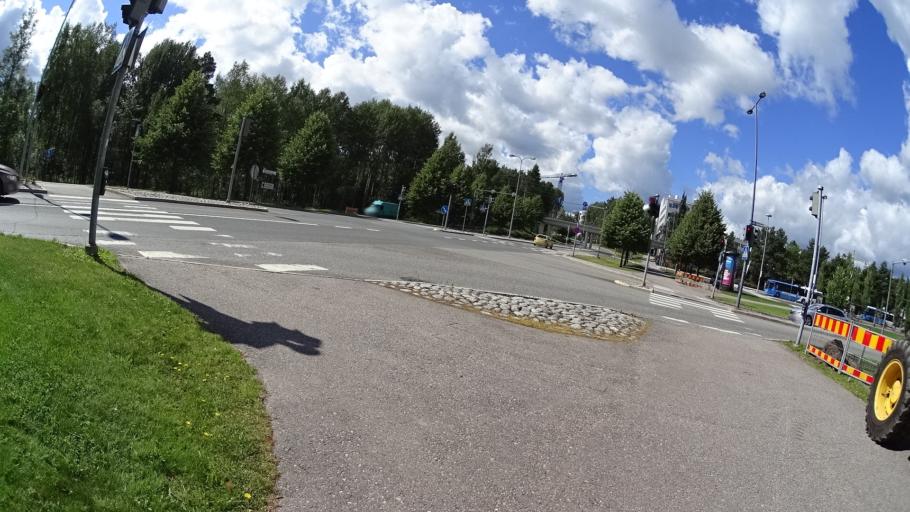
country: FI
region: Uusimaa
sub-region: Helsinki
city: Teekkarikylae
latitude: 60.2767
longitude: 24.8546
